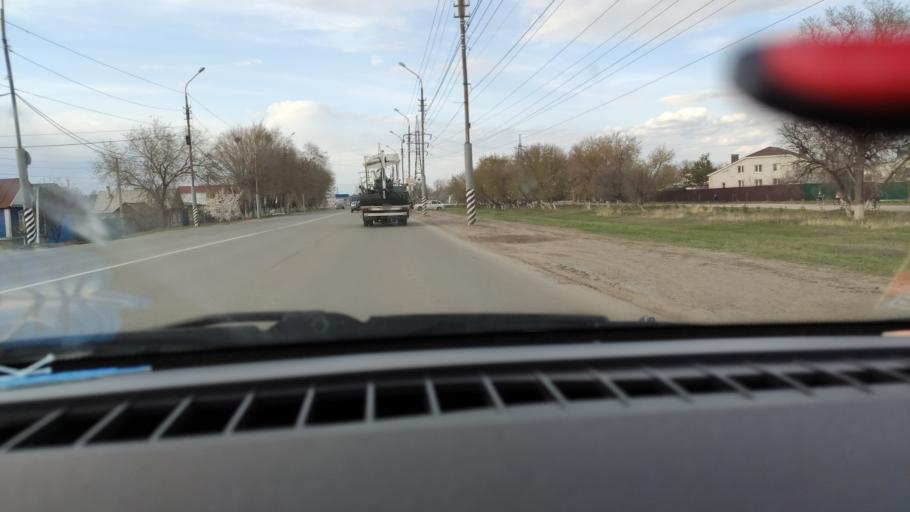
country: RU
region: Saratov
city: Privolzhskiy
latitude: 51.4218
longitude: 46.0473
